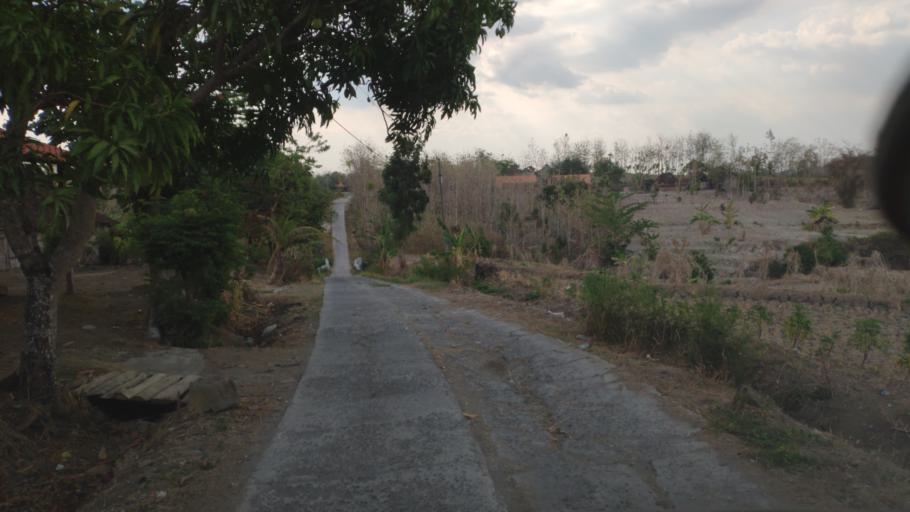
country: ID
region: Central Java
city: Randublatung
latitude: -7.2907
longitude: 111.3150
